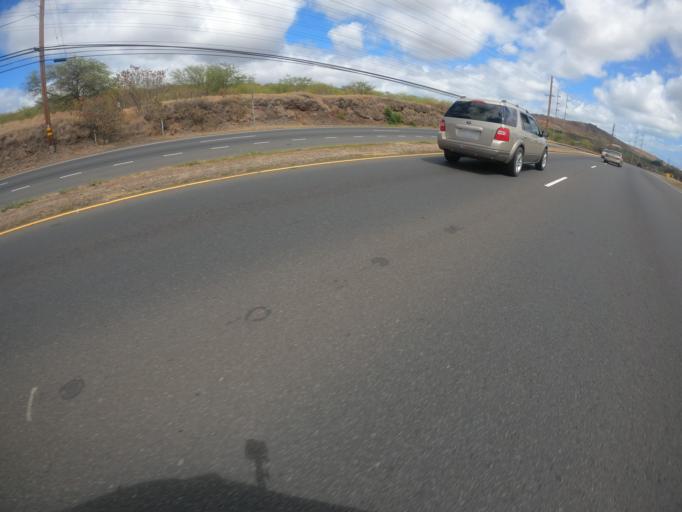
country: US
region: Hawaii
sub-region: Honolulu County
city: Makakilo City
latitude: 21.3415
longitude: -158.1059
